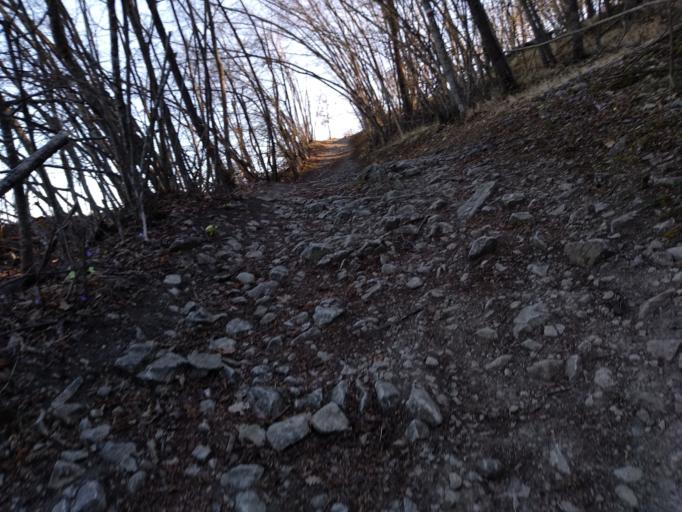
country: IT
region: Emilia-Romagna
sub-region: Provincia di Reggio Emilia
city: Castelnovo ne'Monti
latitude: 44.4223
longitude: 10.4195
